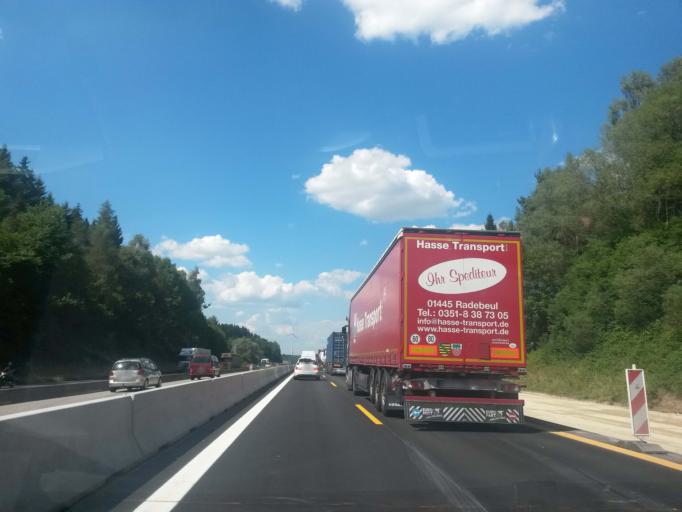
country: DE
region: Bavaria
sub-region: Upper Bavaria
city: Allershausen
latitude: 48.4492
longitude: 11.5903
